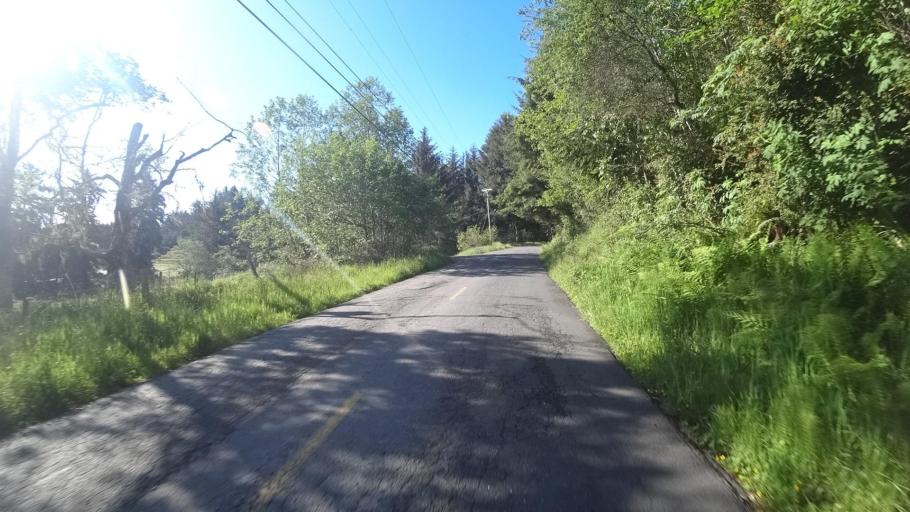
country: US
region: California
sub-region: Humboldt County
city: Westhaven-Moonstone
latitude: 41.0090
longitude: -124.1065
